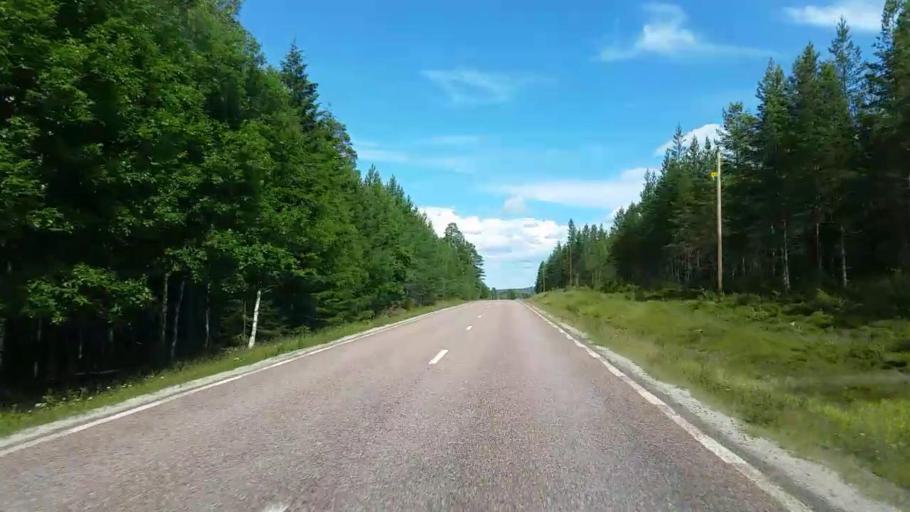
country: SE
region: Dalarna
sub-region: Rattviks Kommun
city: Raettvik
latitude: 61.2032
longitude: 15.3545
